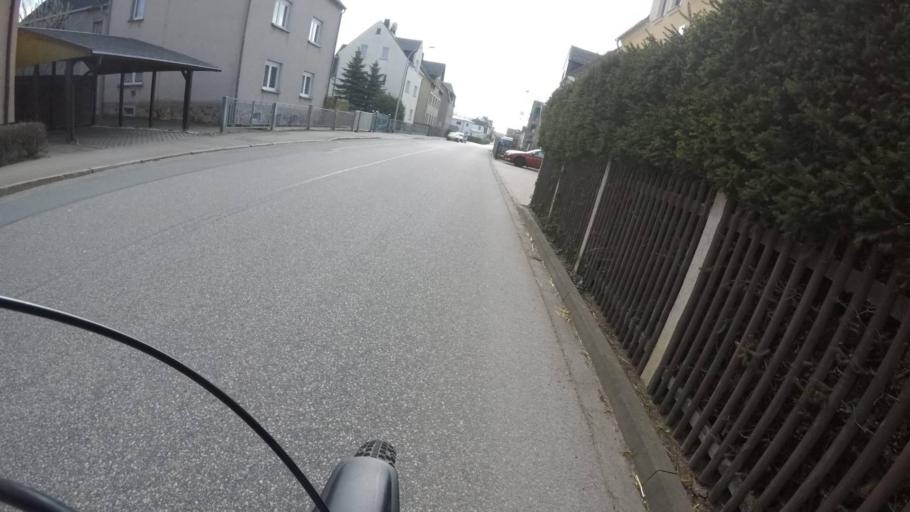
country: DE
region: Saxony
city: Limbach-Oberfrohna
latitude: 50.8487
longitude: 12.7316
